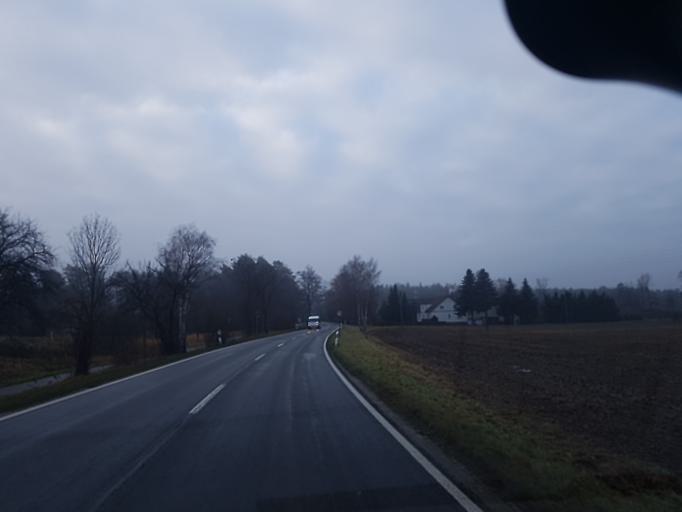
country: DE
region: Brandenburg
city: Finsterwalde
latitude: 51.6015
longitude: 13.7130
